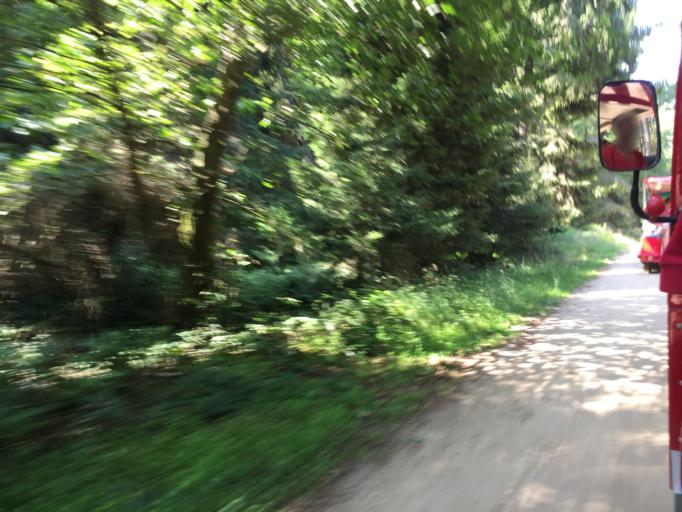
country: PL
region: Pomeranian Voivodeship
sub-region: Powiat leborski
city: Leba
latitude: 54.7487
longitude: 17.4482
